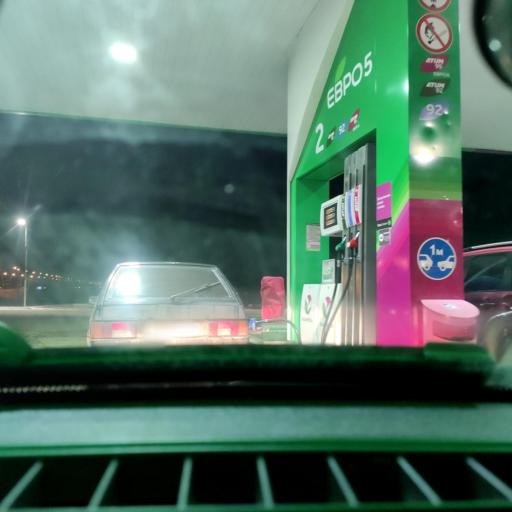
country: RU
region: Bashkortostan
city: Ufa
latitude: 54.8055
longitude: 56.1778
